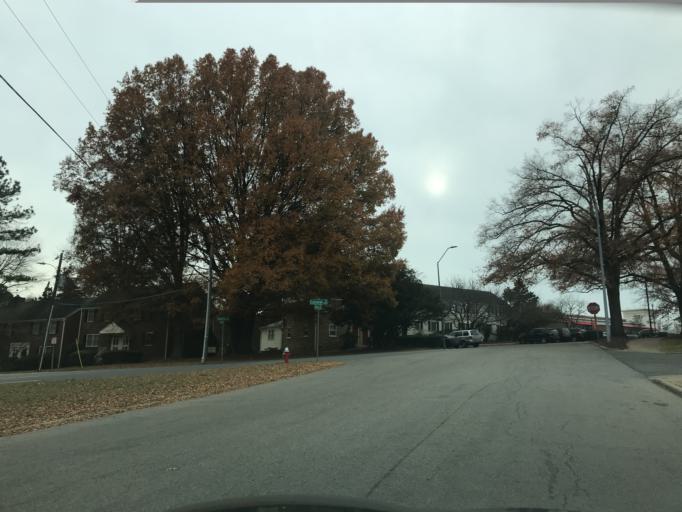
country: US
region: North Carolina
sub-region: Wake County
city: West Raleigh
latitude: 35.7913
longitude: -78.6574
